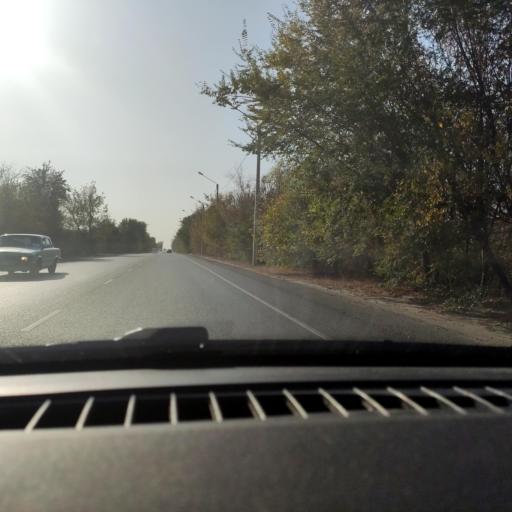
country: RU
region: Voronezj
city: Shilovo
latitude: 51.5774
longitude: 39.1505
